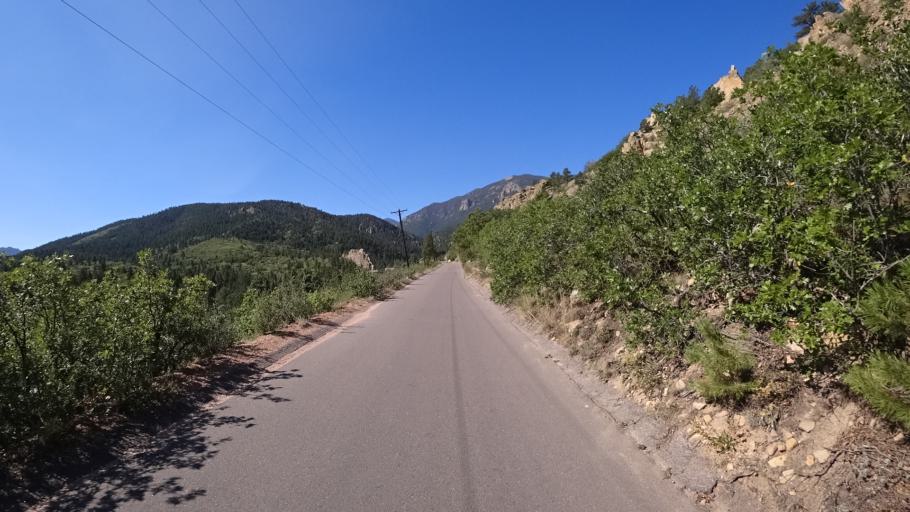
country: US
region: Colorado
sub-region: El Paso County
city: Manitou Springs
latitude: 38.8261
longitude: -104.8850
